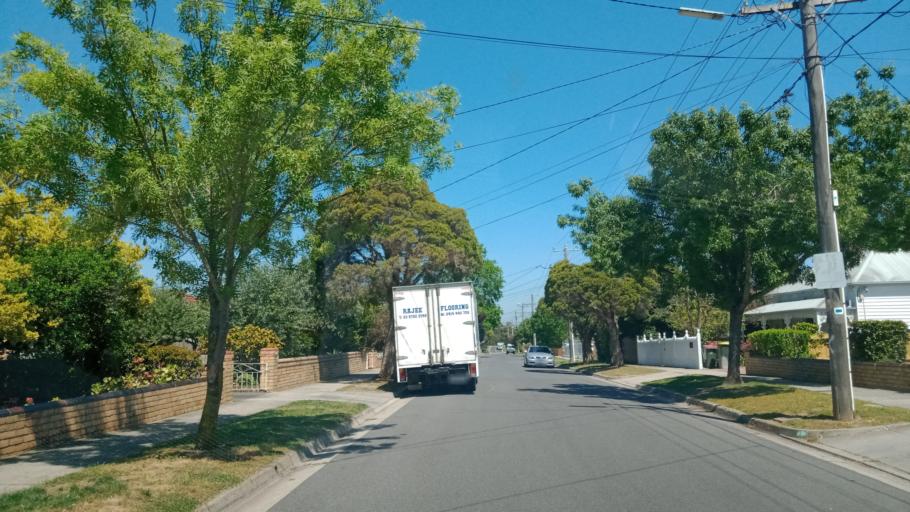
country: AU
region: Victoria
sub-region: Monash
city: Oakleigh South
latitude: -37.9247
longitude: 145.0750
